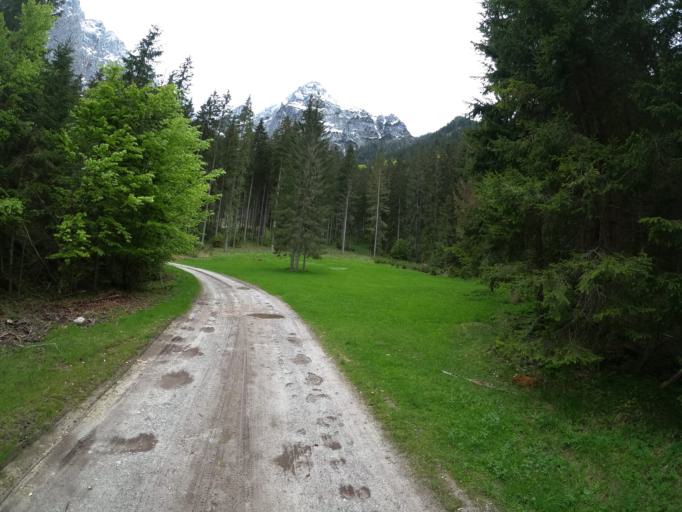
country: AT
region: Salzburg
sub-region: Politischer Bezirk Sankt Johann im Pongau
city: Werfen
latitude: 47.4676
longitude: 13.0798
